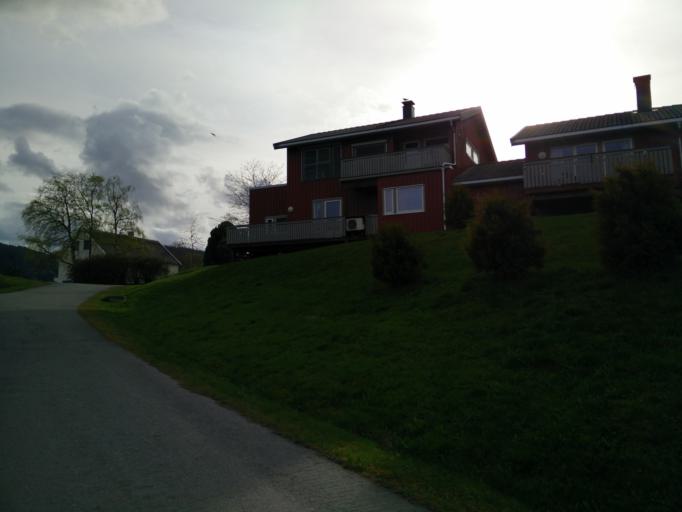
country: NO
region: Sor-Trondelag
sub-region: Skaun
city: Borsa
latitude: 63.3277
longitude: 10.0683
